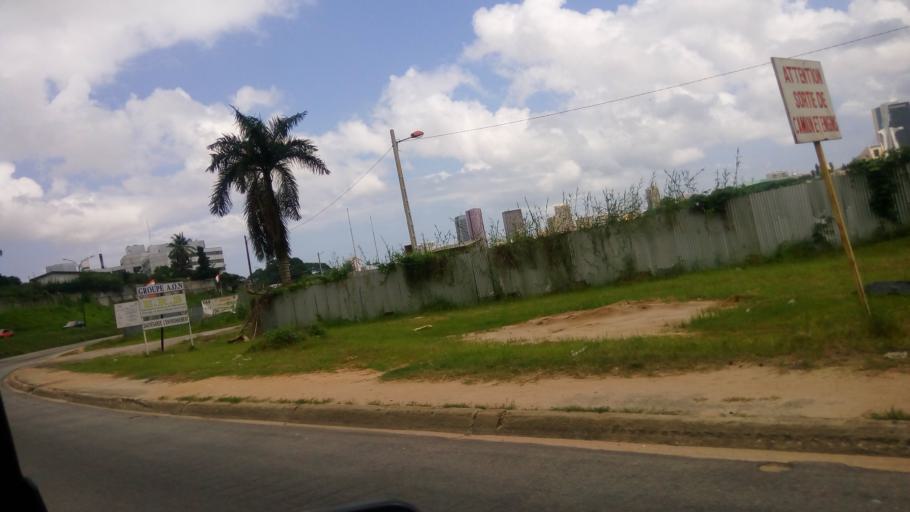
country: CI
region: Lagunes
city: Abidjan
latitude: 5.3398
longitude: -4.0141
